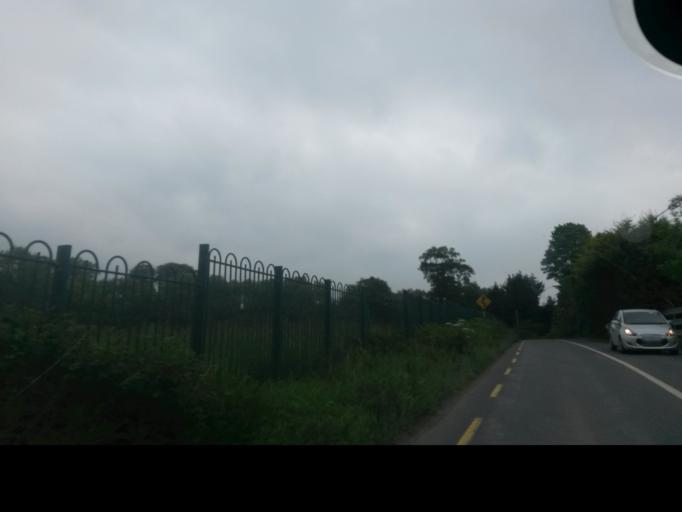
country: IE
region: Leinster
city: Donabate
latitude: 53.4827
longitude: -6.1557
